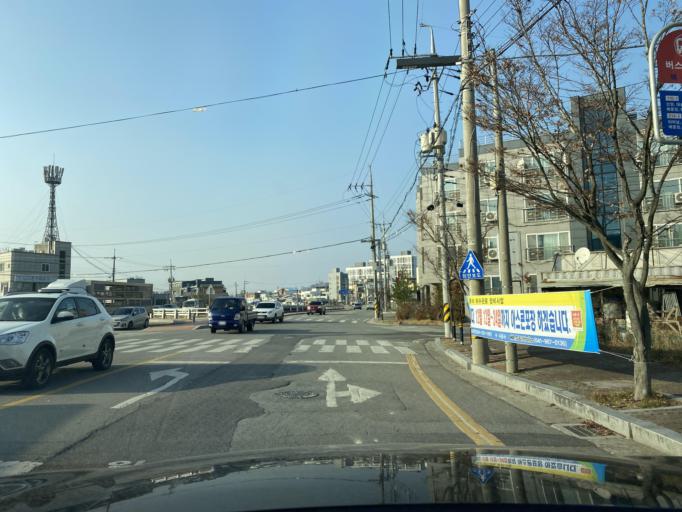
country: KR
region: Chungcheongnam-do
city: Yesan
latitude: 36.6792
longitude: 126.8347
